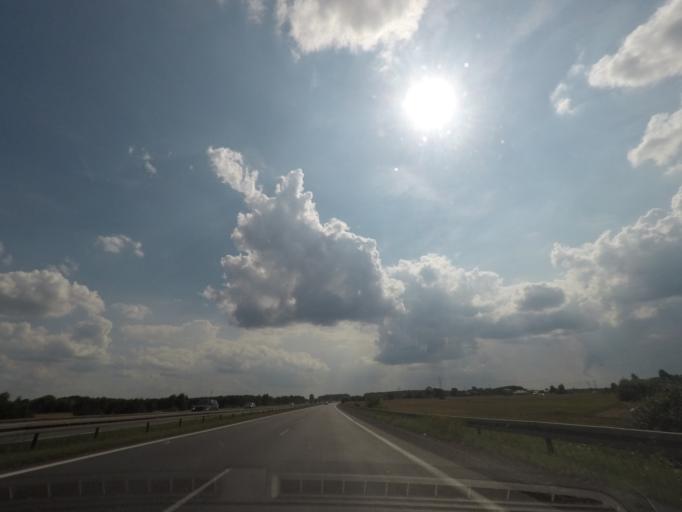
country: PL
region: Lodz Voivodeship
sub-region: Powiat piotrkowski
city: Wola Krzysztoporska
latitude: 51.3144
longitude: 19.5727
